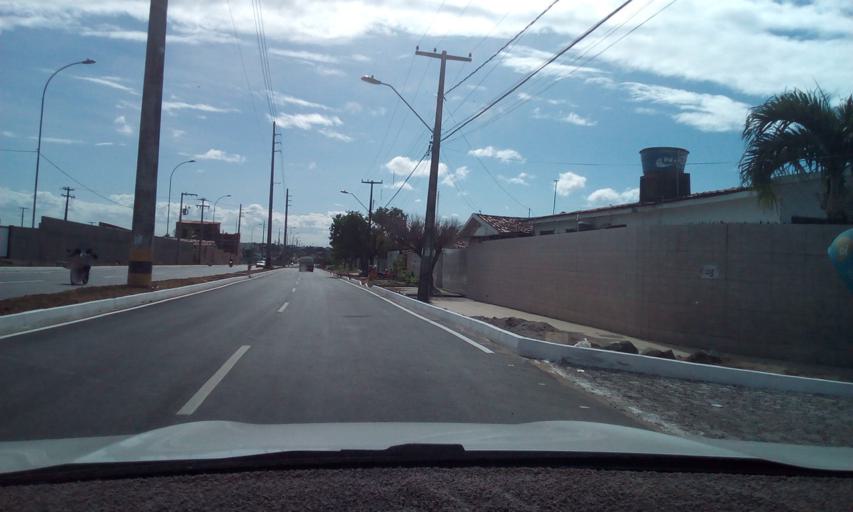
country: BR
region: Paraiba
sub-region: Conde
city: Conde
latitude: -7.2085
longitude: -34.8432
